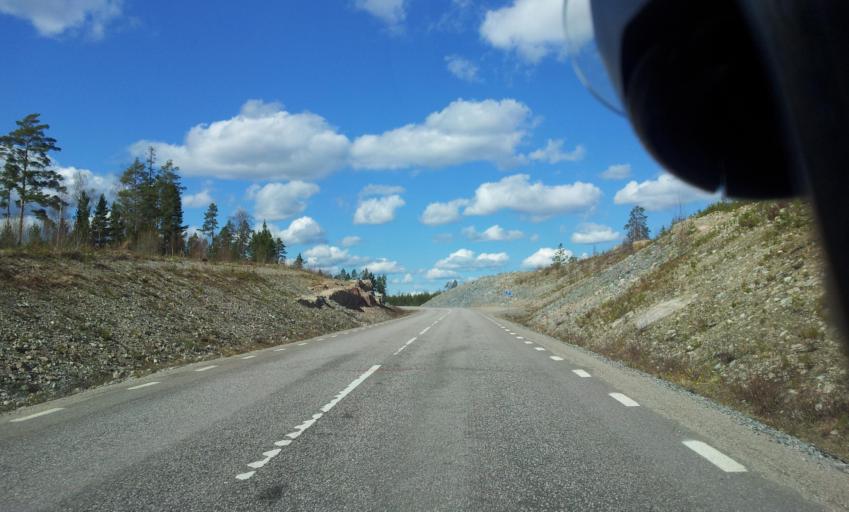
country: SE
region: Gaevleborg
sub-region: Ovanakers Kommun
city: Edsbyn
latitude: 61.2320
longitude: 15.8841
